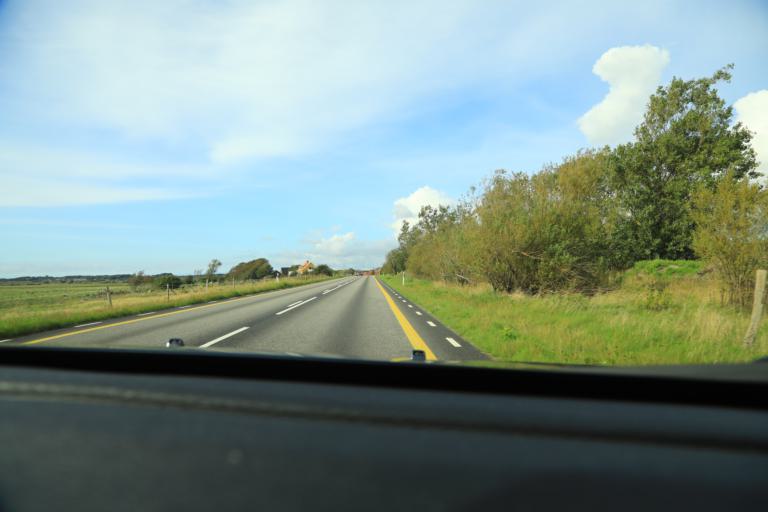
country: SE
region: Halland
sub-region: Varbergs Kommun
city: Traslovslage
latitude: 57.0294
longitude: 12.3321
